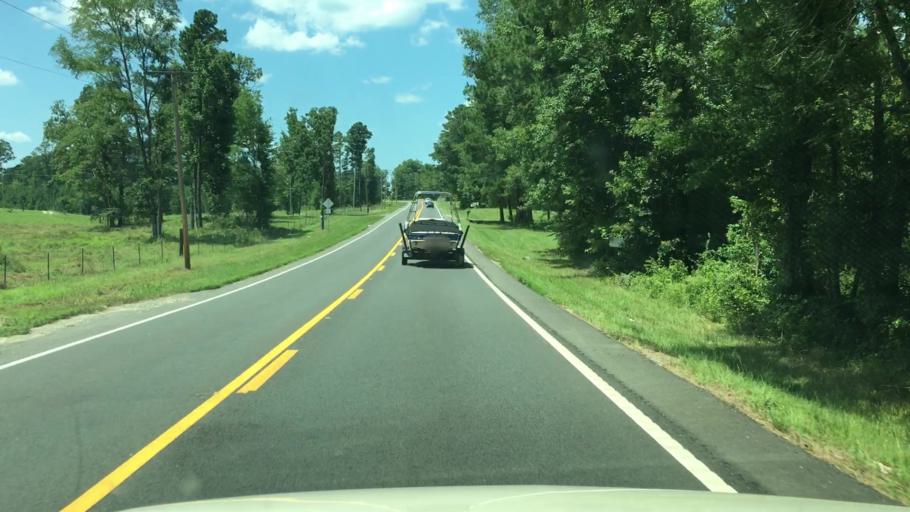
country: US
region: Arkansas
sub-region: Garland County
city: Lake Hamilton
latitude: 34.2741
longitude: -93.1494
